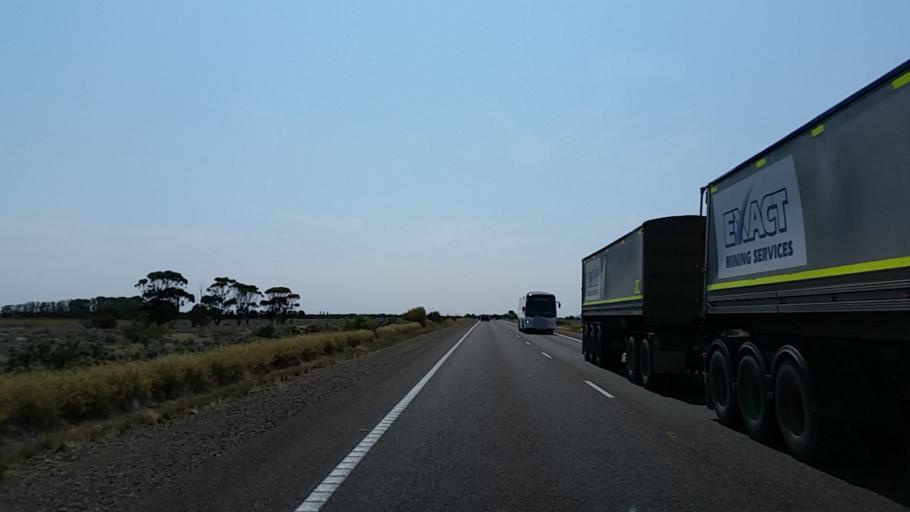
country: AU
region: South Australia
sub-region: Port Augusta
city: Port Augusta
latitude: -32.7355
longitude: 137.9413
